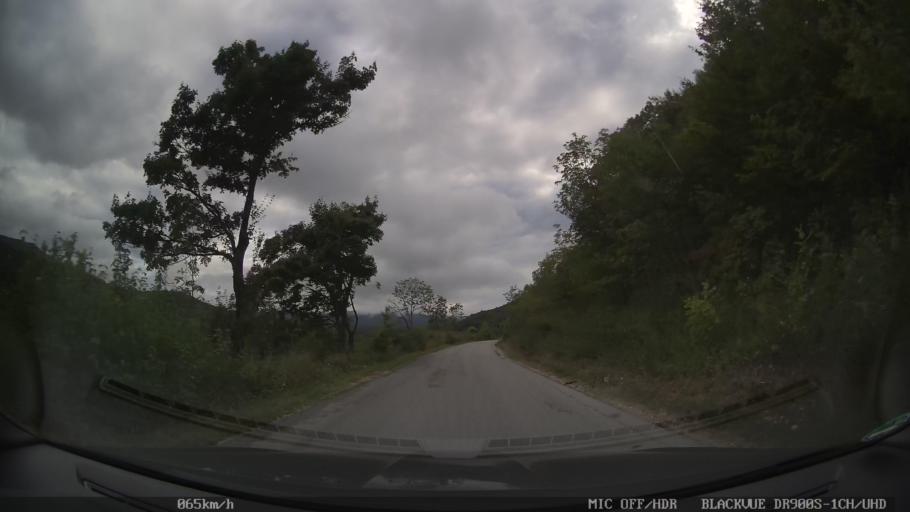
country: HR
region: Licko-Senjska
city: Jezerce
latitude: 44.9294
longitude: 15.6206
